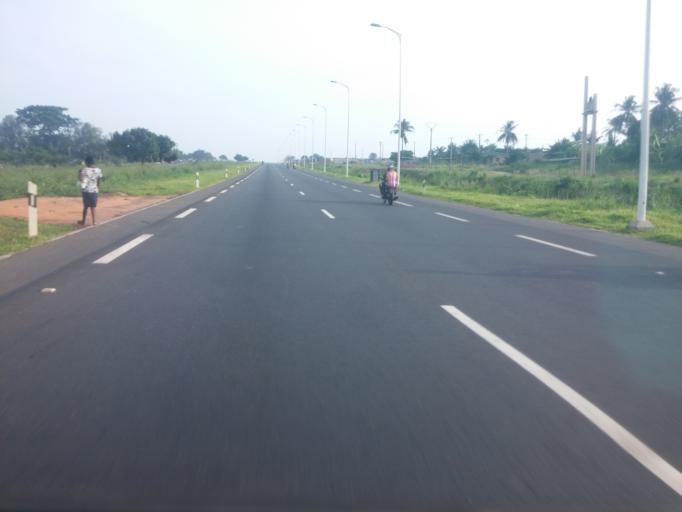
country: TG
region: Maritime
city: Tsevie
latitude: 6.3356
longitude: 1.2165
